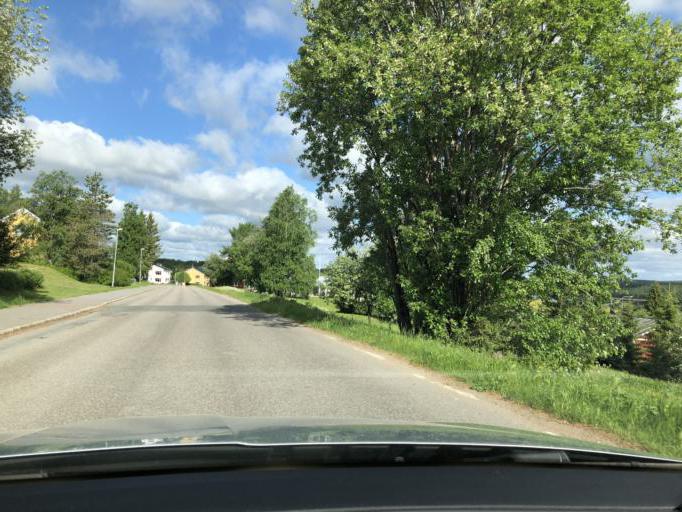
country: SE
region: Norrbotten
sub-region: Pajala Kommun
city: Pajala
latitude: 67.2167
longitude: 23.3626
